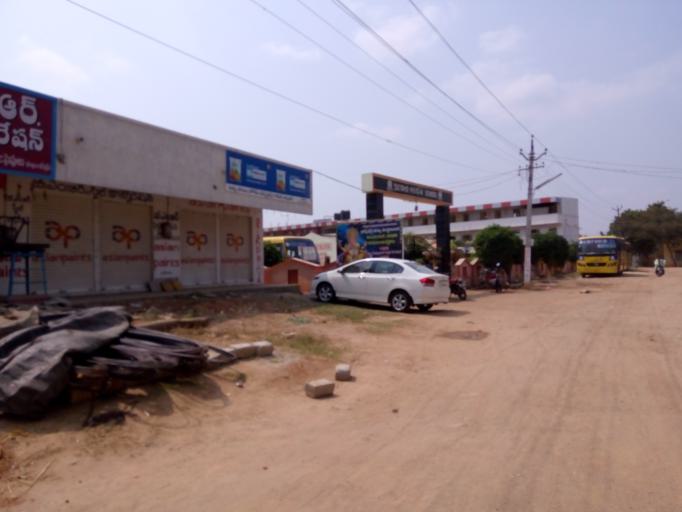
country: IN
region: Andhra Pradesh
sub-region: Prakasam
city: pedda nakkalapalem
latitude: 15.9671
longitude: 80.2743
